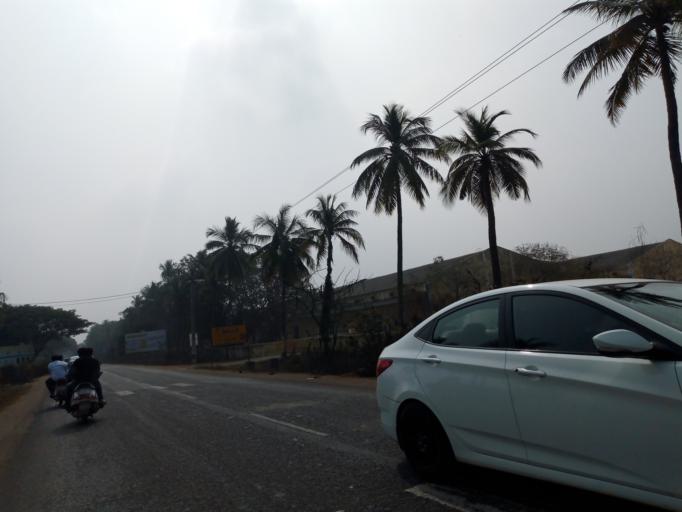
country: IN
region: Andhra Pradesh
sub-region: West Godavari
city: Bhimavaram
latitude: 16.5770
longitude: 81.4791
